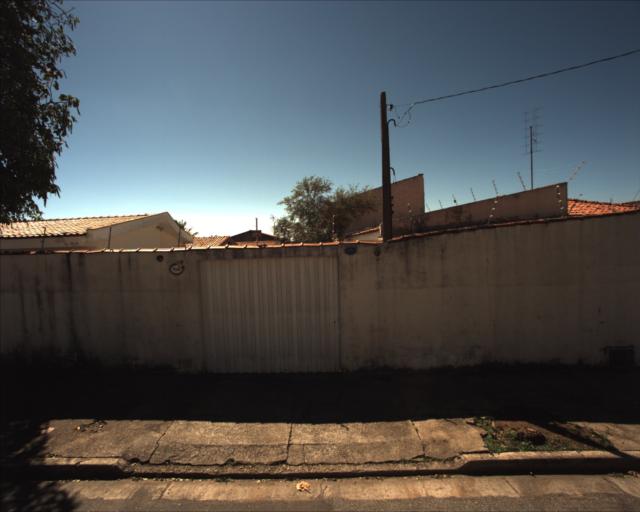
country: BR
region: Sao Paulo
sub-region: Sorocaba
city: Sorocaba
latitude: -23.5058
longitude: -47.4877
